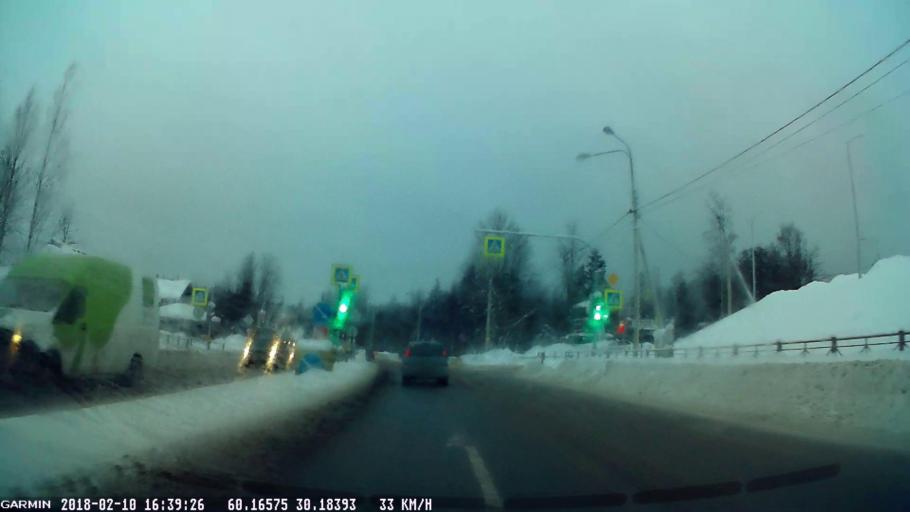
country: RU
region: Leningrad
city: Sertolovo
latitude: 60.1569
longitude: 30.1889
